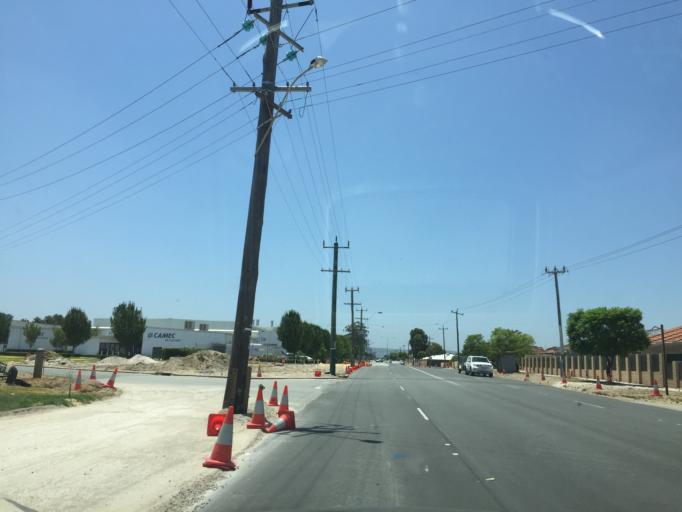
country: AU
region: Western Australia
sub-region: Canning
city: Queens Park
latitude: -31.9959
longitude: 115.9402
